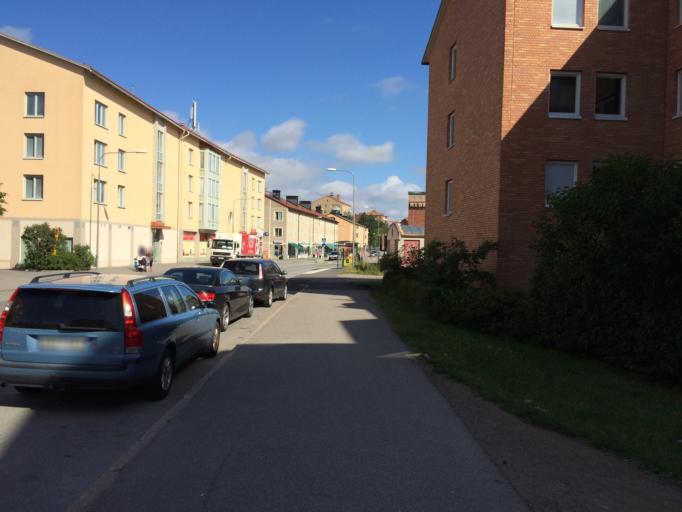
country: SE
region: Stockholm
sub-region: Huddinge Kommun
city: Segeltorp
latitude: 59.2964
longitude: 17.9834
